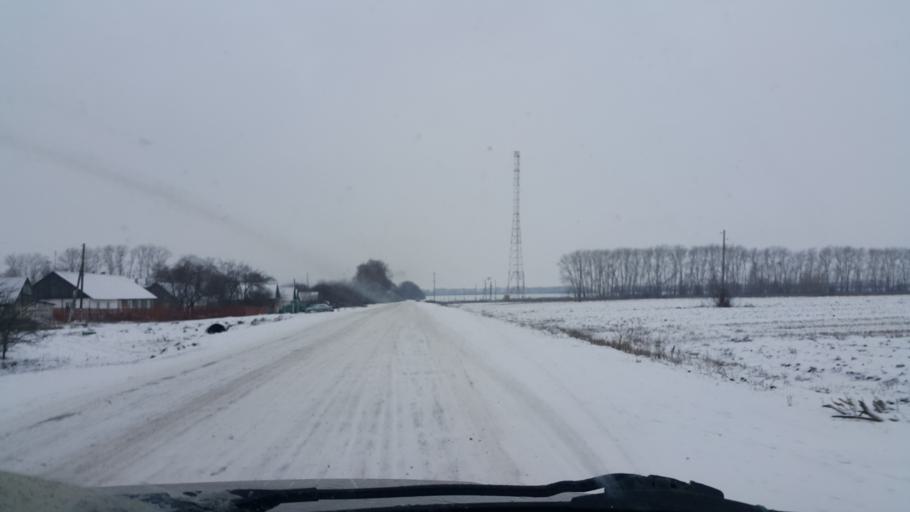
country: RU
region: Tambov
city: Inzhavino
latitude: 52.4691
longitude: 42.3866
